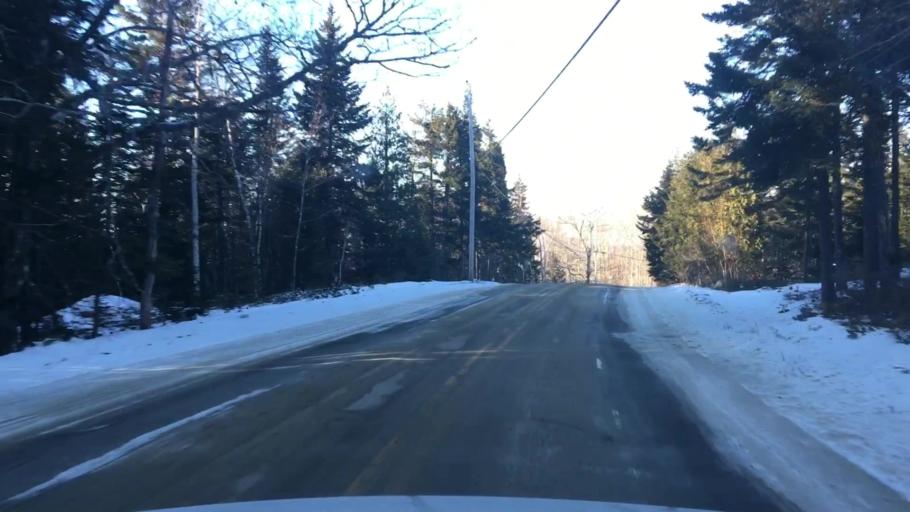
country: US
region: Maine
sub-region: Hancock County
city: Castine
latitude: 44.3675
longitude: -68.7532
